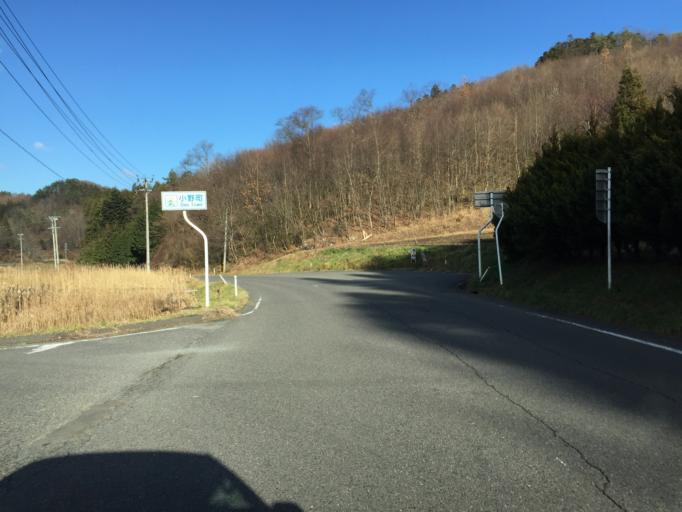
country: JP
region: Fukushima
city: Ishikawa
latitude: 37.2232
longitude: 140.6002
